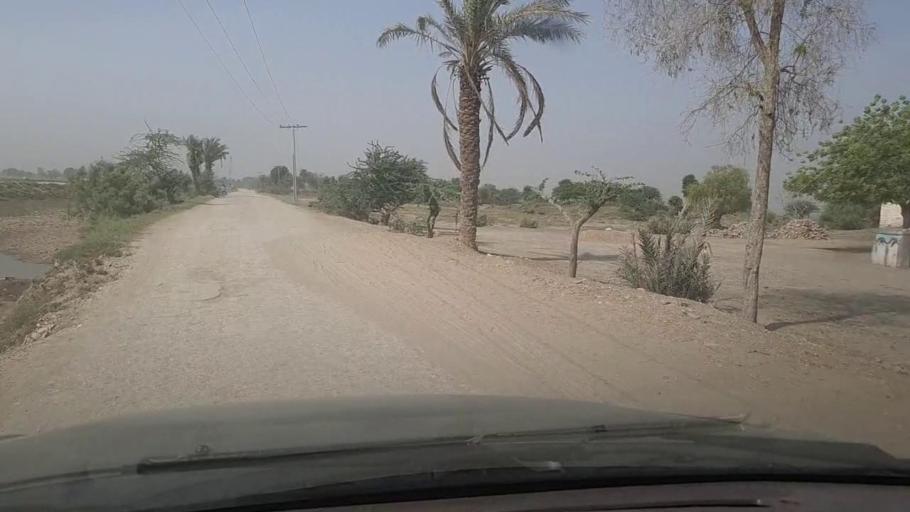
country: PK
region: Sindh
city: Garhi Yasin
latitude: 27.8689
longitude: 68.5563
